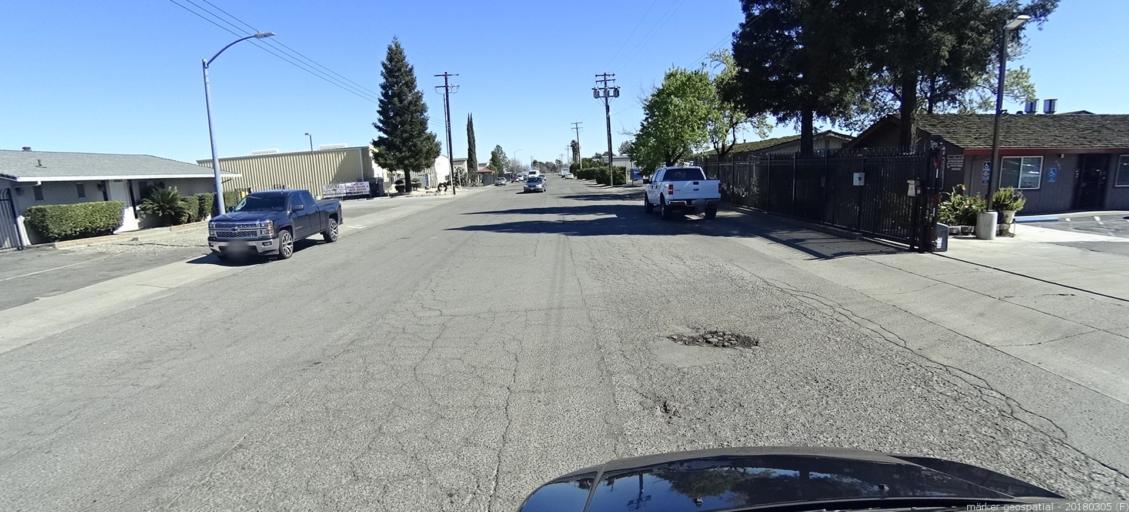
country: US
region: California
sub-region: Sacramento County
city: Florin
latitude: 38.4997
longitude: -121.3885
